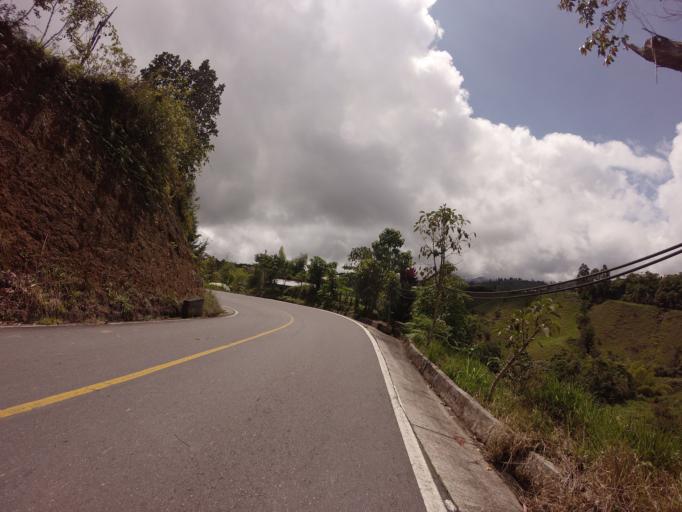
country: CO
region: Caldas
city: Marquetalia
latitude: 5.2756
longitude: -75.1085
